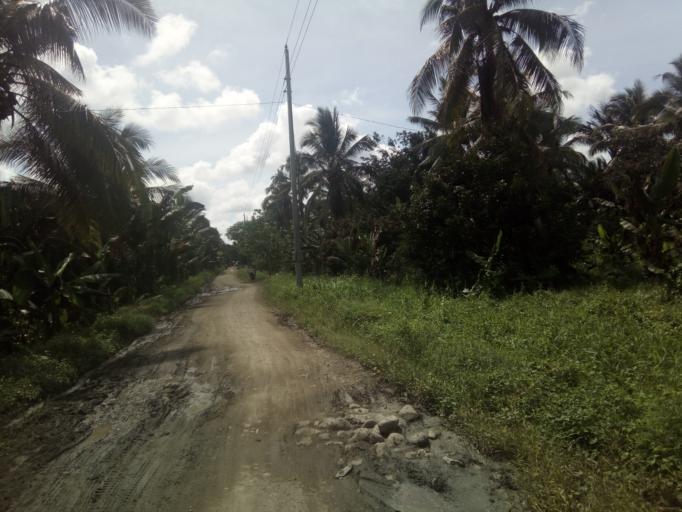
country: PH
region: Caraga
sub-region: Province of Agusan del Sur
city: Santa Josefa
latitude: 8.0373
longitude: 126.0119
